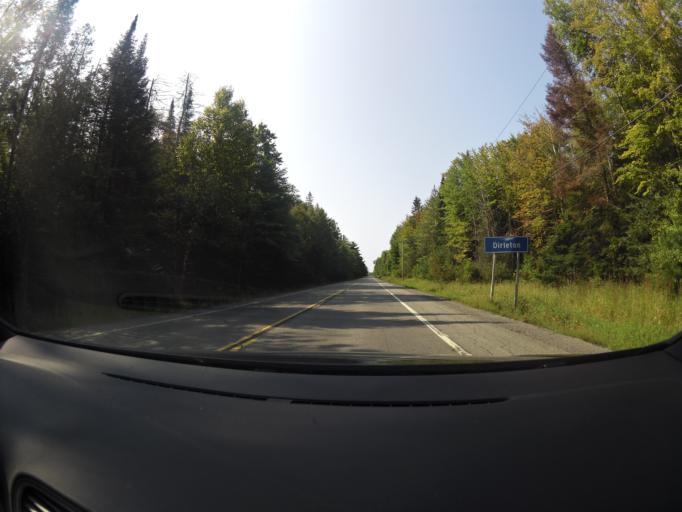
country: CA
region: Ontario
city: Arnprior
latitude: 45.5019
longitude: -76.1313
